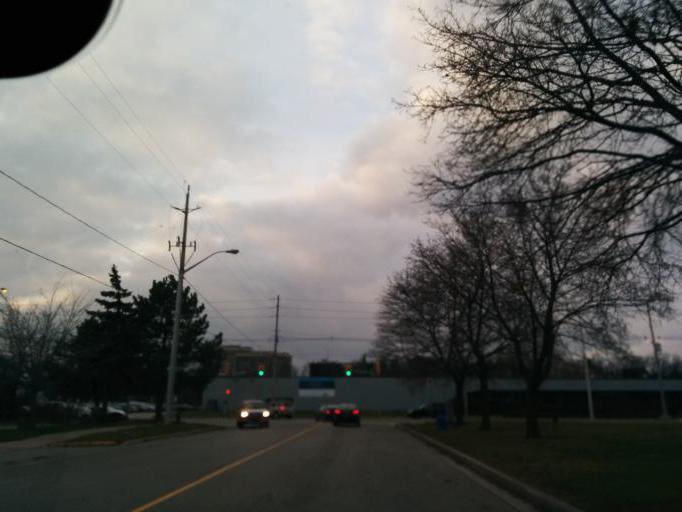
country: CA
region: Ontario
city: Oakville
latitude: 43.4654
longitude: -79.6835
